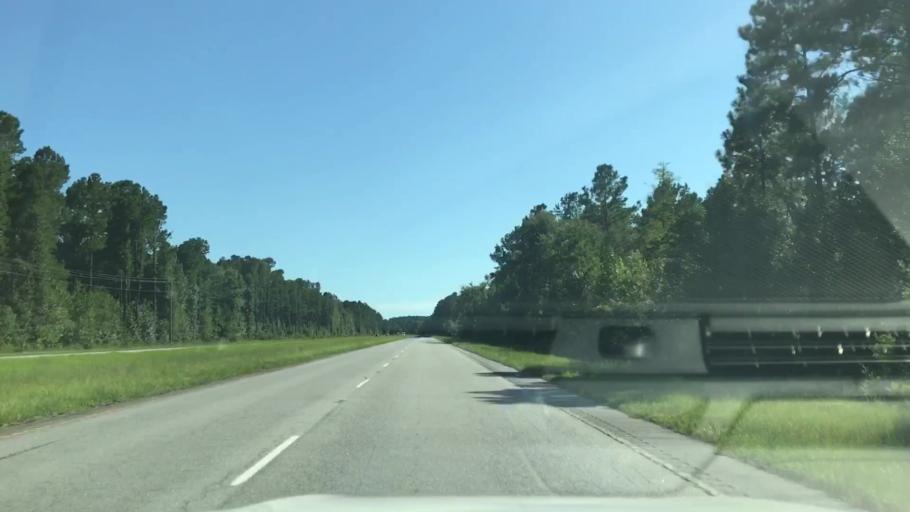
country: US
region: South Carolina
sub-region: Charleston County
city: Awendaw
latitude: 33.0107
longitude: -79.6385
